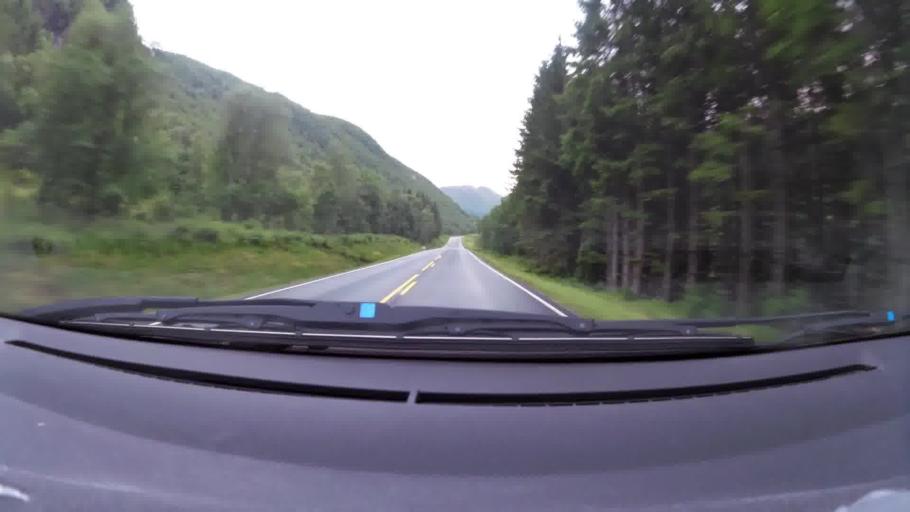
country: NO
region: More og Romsdal
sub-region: Molde
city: Molde
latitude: 62.7986
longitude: 7.3066
